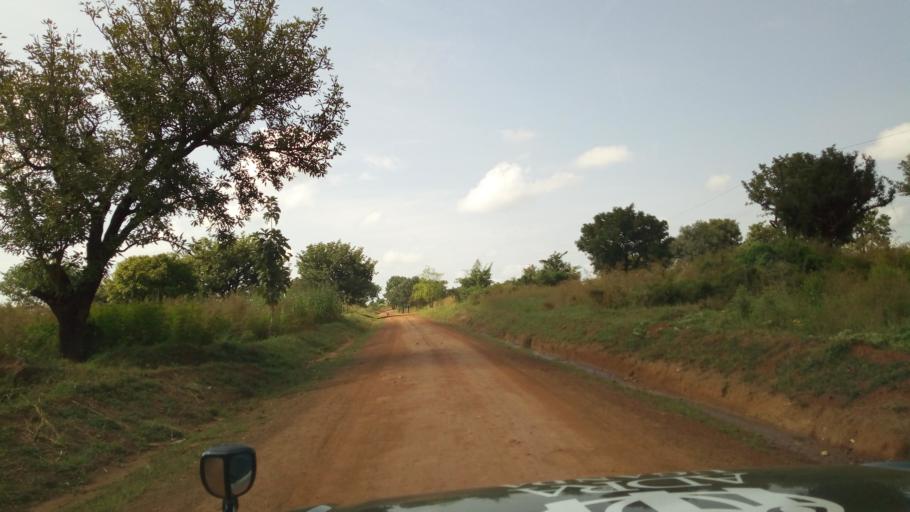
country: UG
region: Northern Region
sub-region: Moyo District
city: Moyo
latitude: 3.5881
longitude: 31.5233
